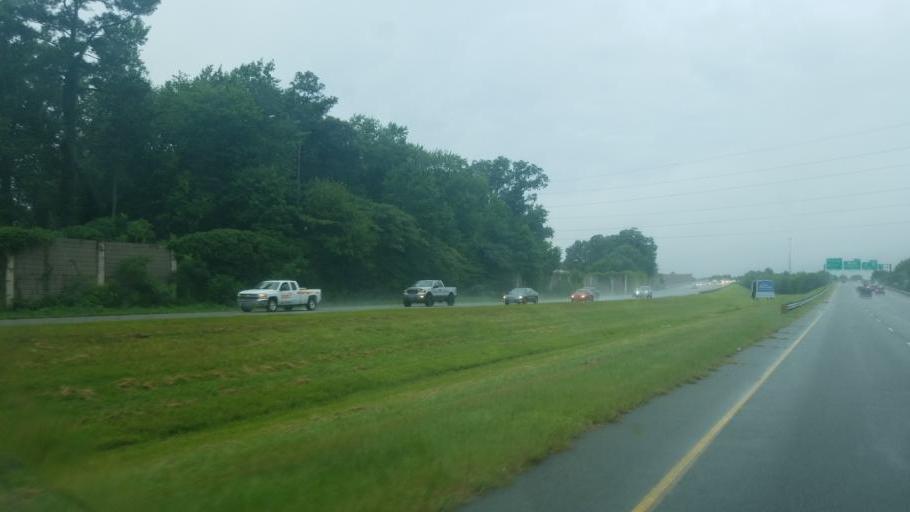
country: US
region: Virginia
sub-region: City of Chesapeake
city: Chesapeake
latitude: 36.7516
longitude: -76.2624
